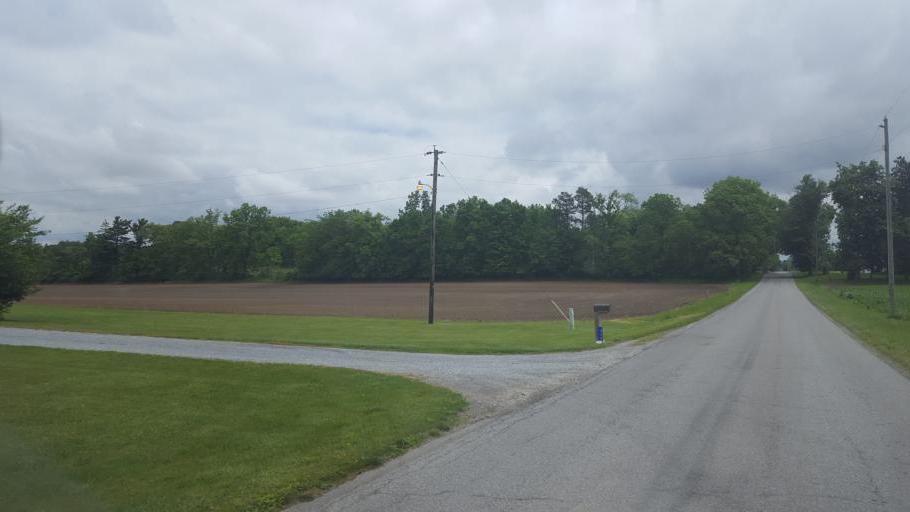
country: US
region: Ohio
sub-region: Crawford County
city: Bucyrus
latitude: 40.7756
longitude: -83.0665
